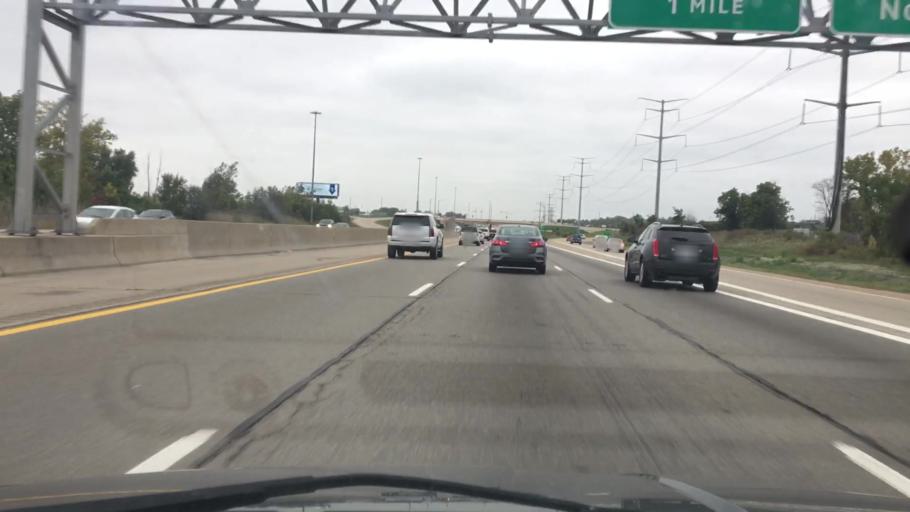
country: US
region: Michigan
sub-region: Oakland County
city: Novi
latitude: 42.4926
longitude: -83.5095
